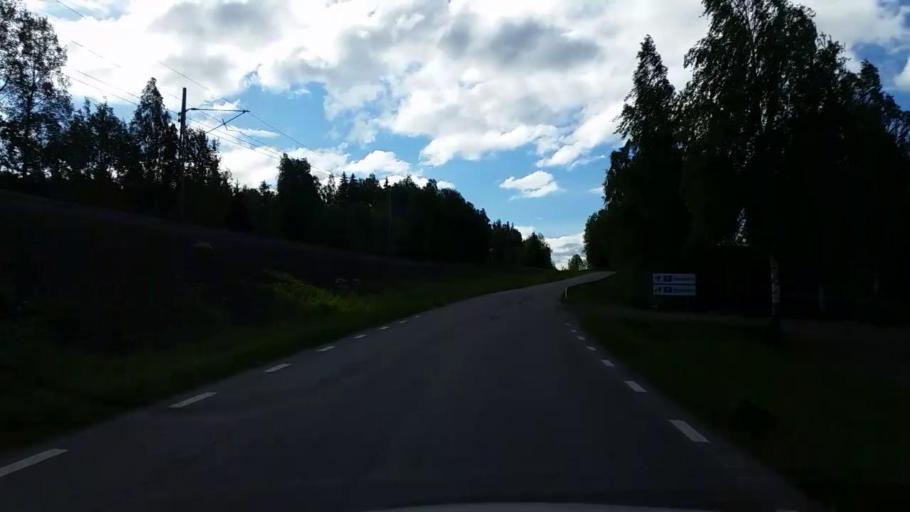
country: SE
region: Dalarna
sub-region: Borlange Kommun
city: Ornas
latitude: 60.5130
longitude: 15.5681
